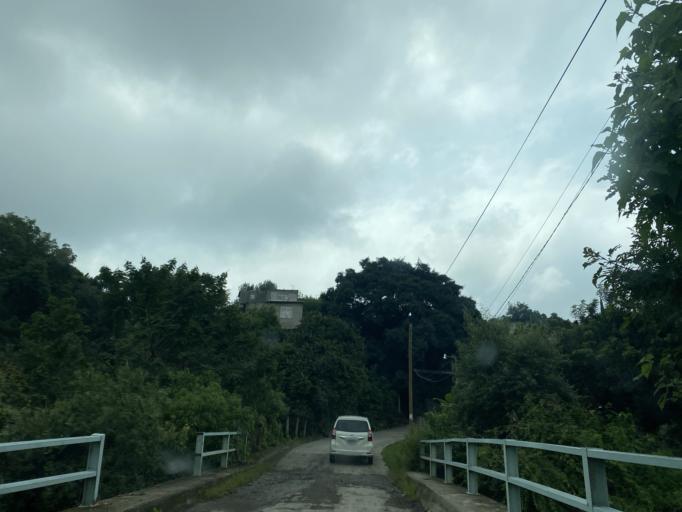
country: MX
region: Morelos
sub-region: Yecapixtla
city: Achichipico
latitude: 18.9527
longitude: -98.8268
